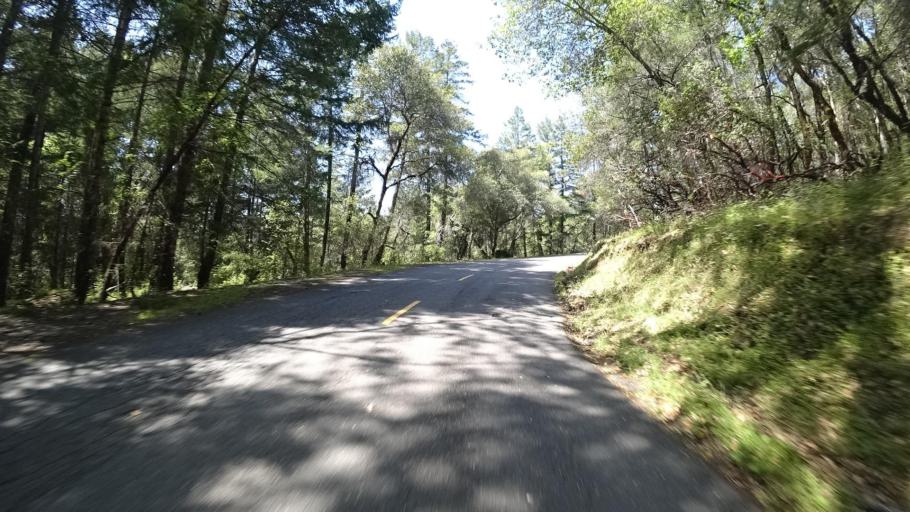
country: US
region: California
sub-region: Humboldt County
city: Redway
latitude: 40.2406
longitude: -123.6250
